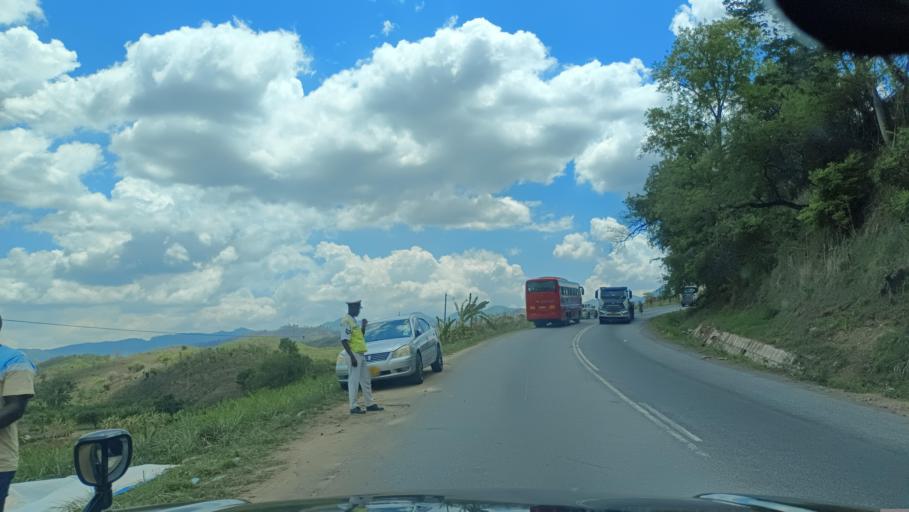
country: TZ
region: Morogoro
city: Mikumi
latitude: -7.4538
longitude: 36.9215
